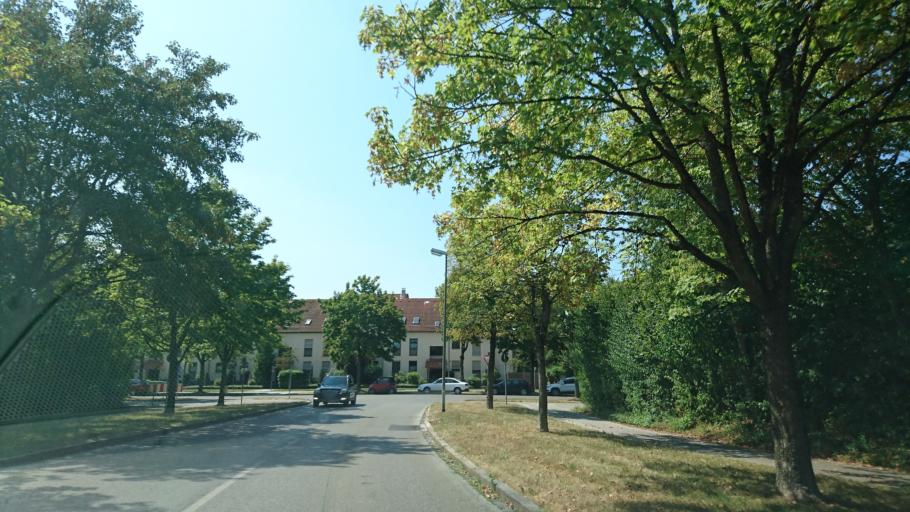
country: DE
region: Bavaria
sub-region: Swabia
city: Friedberg
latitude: 48.3396
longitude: 10.9509
